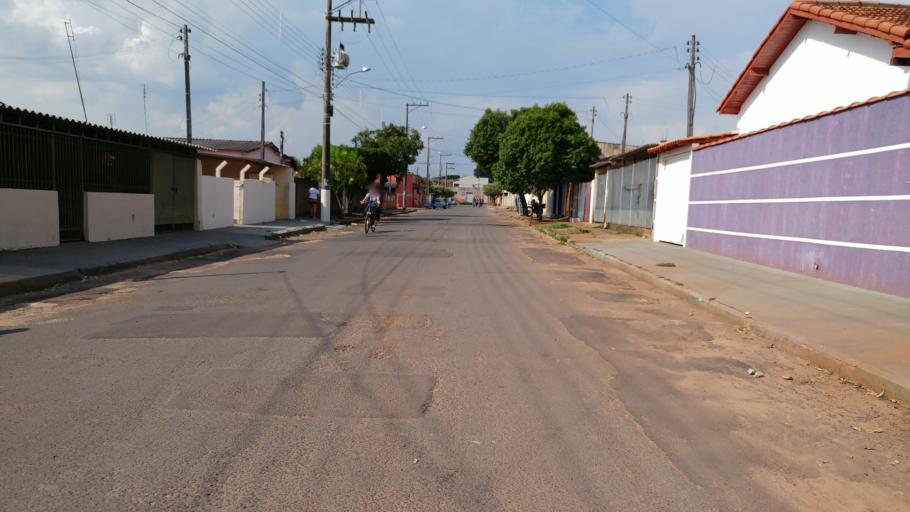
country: BR
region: Sao Paulo
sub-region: Paraguacu Paulista
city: Paraguacu Paulista
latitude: -22.4225
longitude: -50.5866
